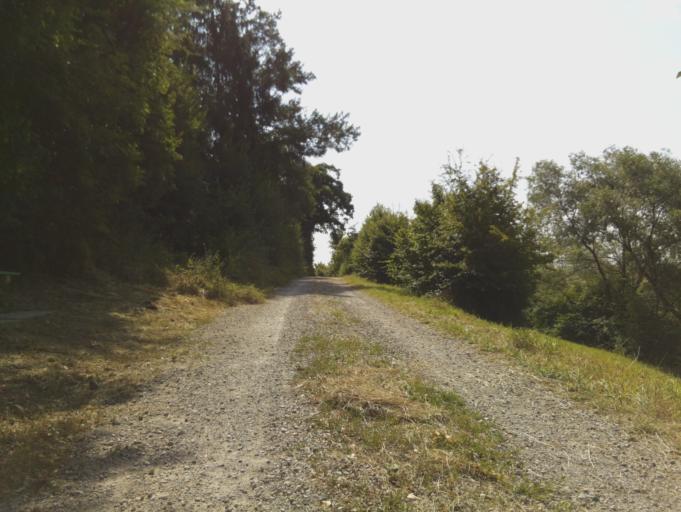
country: CH
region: Zurich
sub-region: Bezirk Andelfingen
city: Henggart
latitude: 47.5779
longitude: 8.6753
